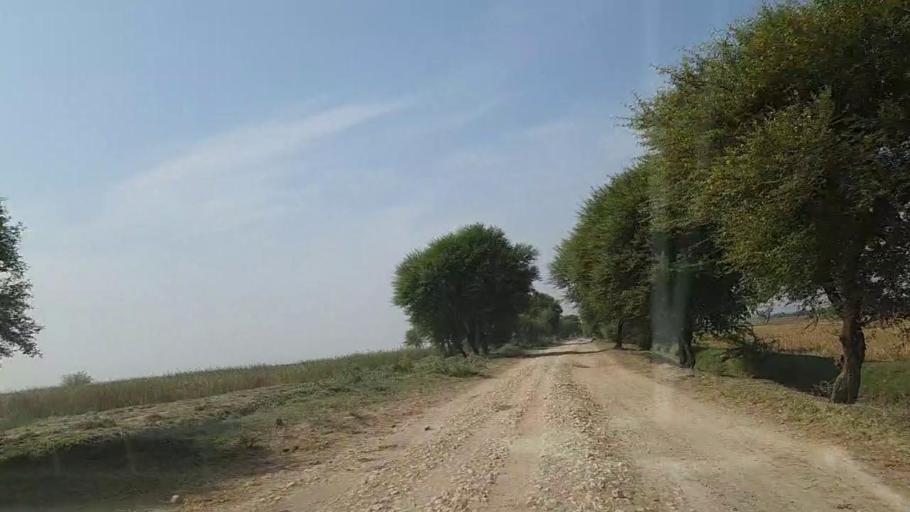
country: PK
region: Sindh
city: Mirpur Batoro
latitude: 24.6111
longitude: 68.2330
